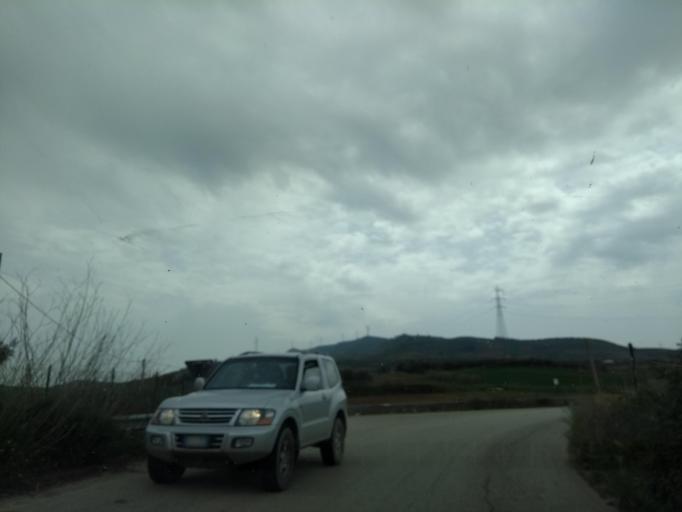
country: IT
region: Sicily
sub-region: Palermo
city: Partinico
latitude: 37.9908
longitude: 13.0678
